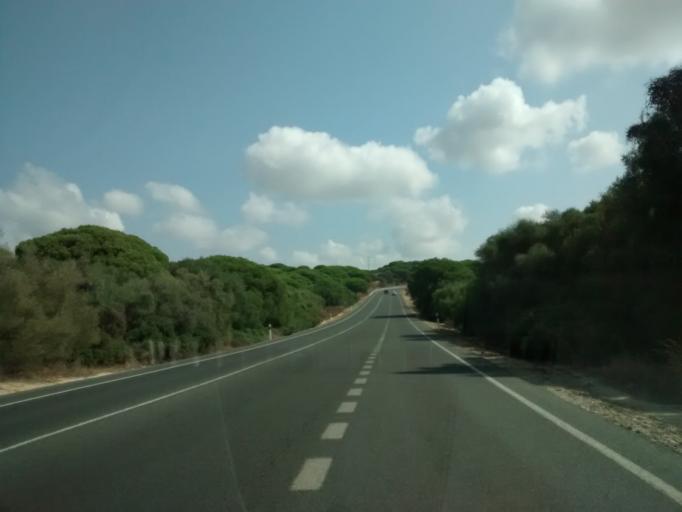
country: ES
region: Andalusia
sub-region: Provincia de Cadiz
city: Vejer de la Frontera
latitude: 36.2531
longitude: -5.9505
